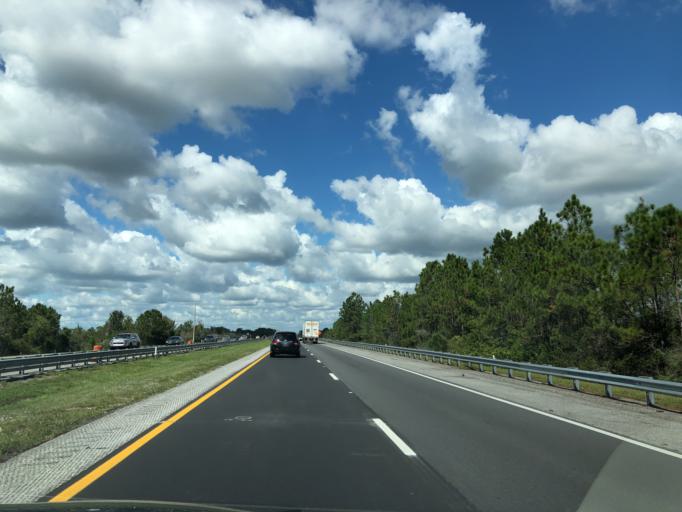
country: US
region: Florida
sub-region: Brevard County
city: June Park
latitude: 27.9036
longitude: -81.0458
